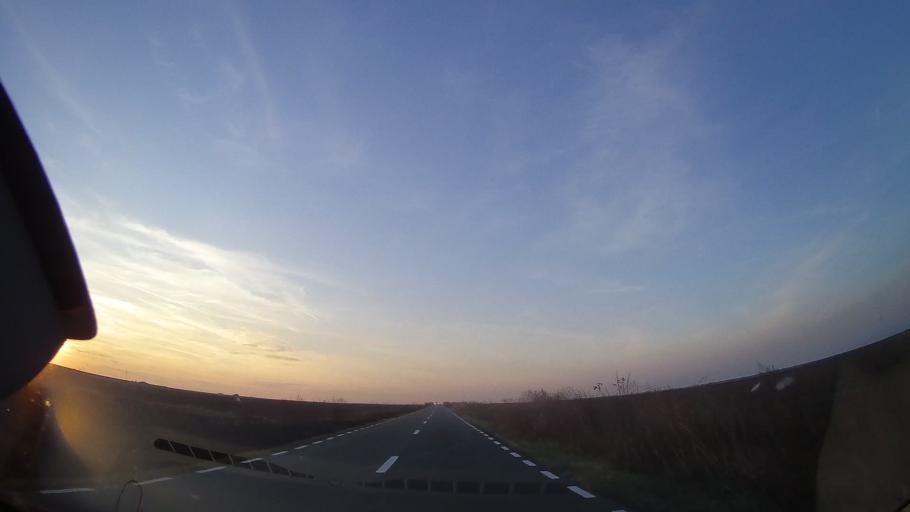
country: RO
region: Constanta
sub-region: Comuna Topraisar
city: Topraisar
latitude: 44.0217
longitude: 28.4140
